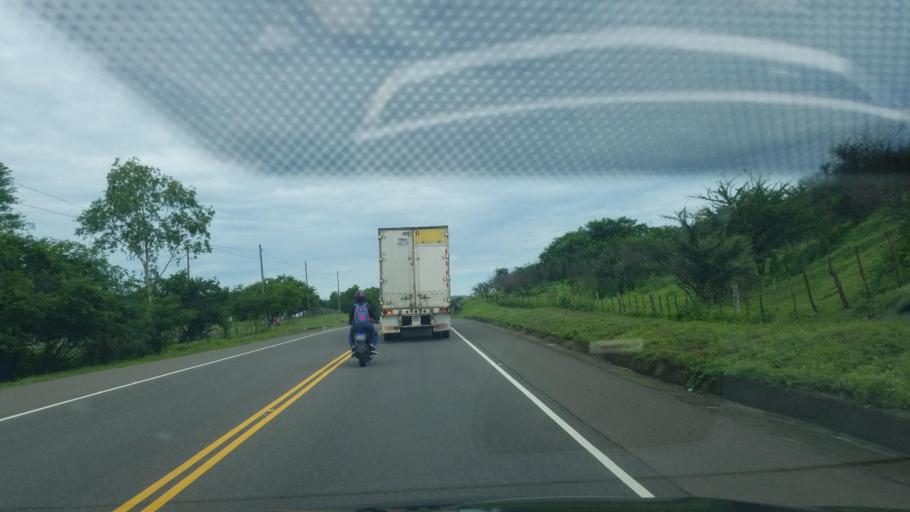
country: HN
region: Valle
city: Goascoran
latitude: 13.5393
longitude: -87.6104
